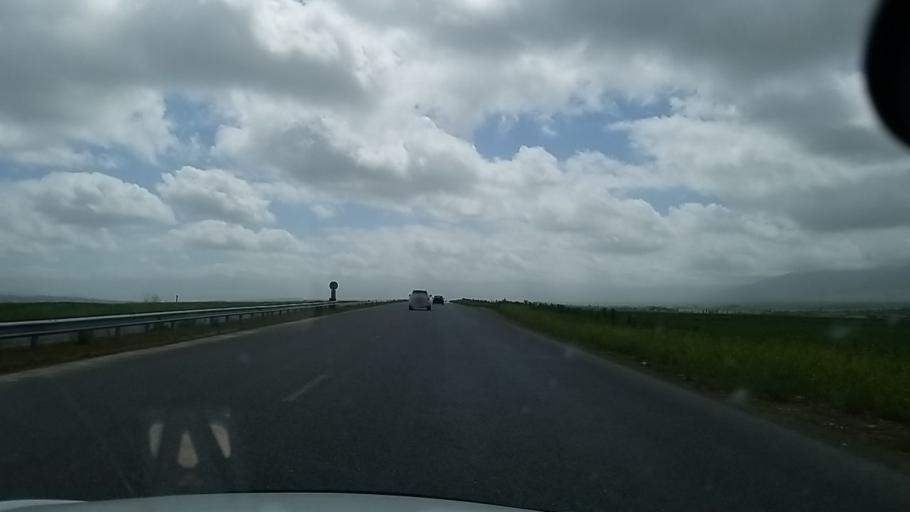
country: KZ
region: Ongtustik Qazaqstan
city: Kokterek
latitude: 42.5412
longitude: 70.2823
